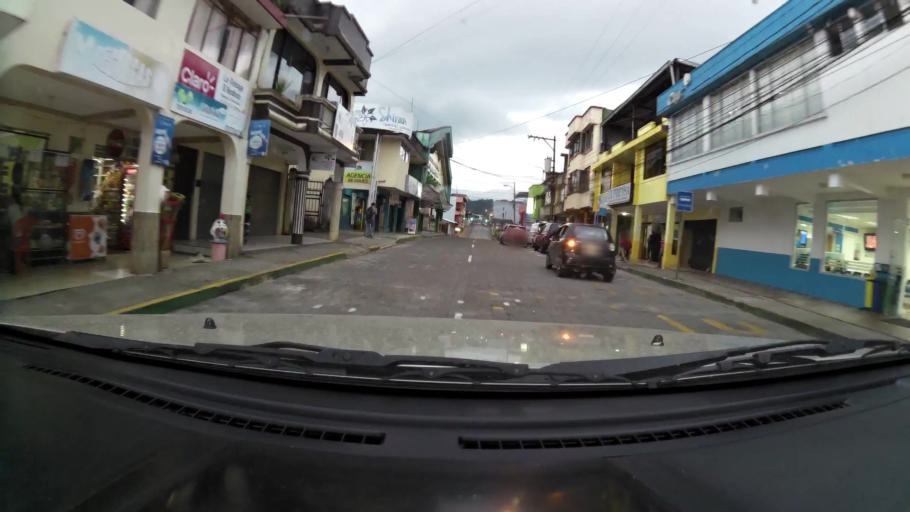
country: EC
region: Pastaza
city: Puyo
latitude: -1.4869
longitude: -78.0002
